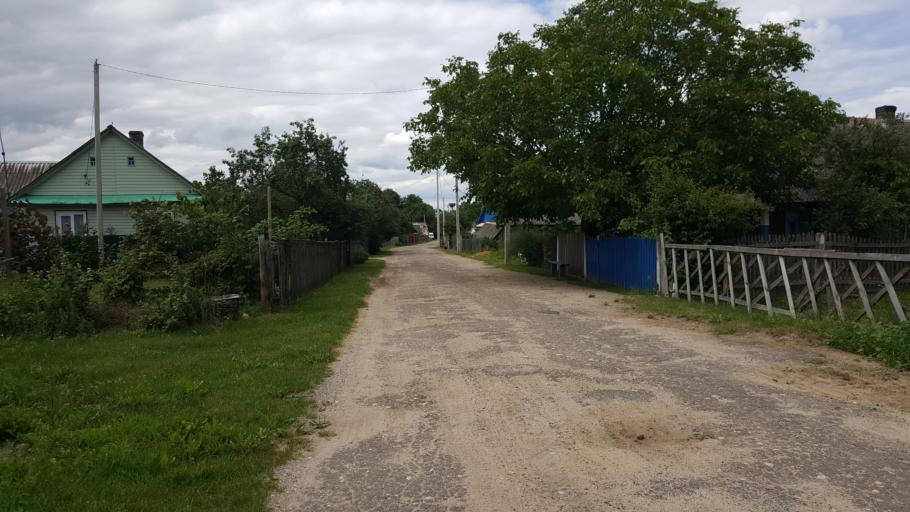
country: BY
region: Brest
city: Kamyanyets
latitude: 52.3702
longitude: 23.9000
